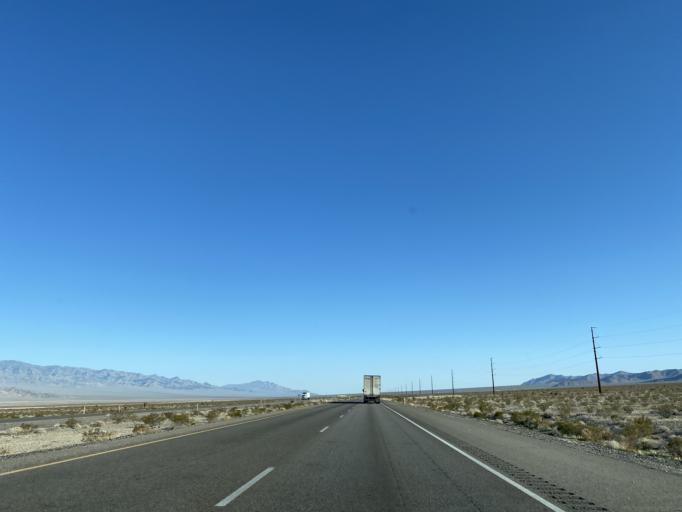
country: US
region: Nevada
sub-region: Clark County
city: Summerlin South
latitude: 36.5508
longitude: -115.5953
